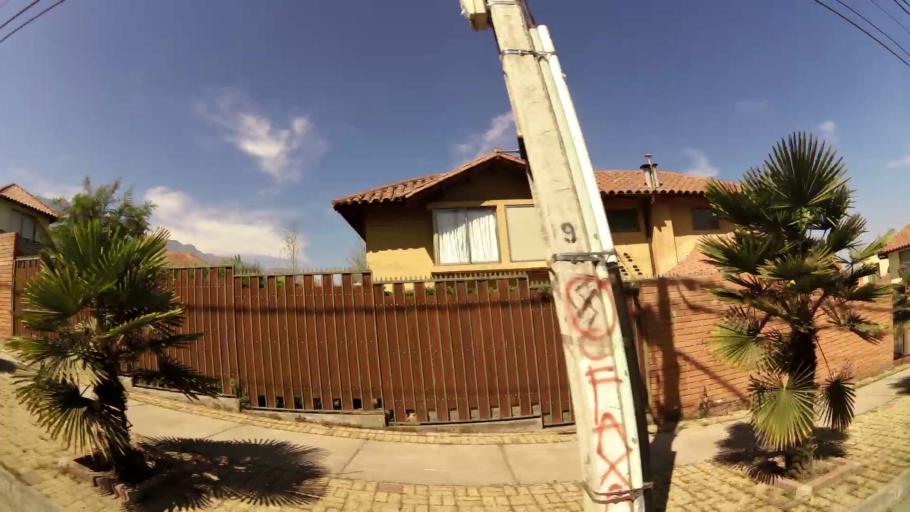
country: CL
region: Santiago Metropolitan
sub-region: Provincia de Santiago
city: Villa Presidente Frei, Nunoa, Santiago, Chile
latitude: -33.4354
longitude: -70.5315
